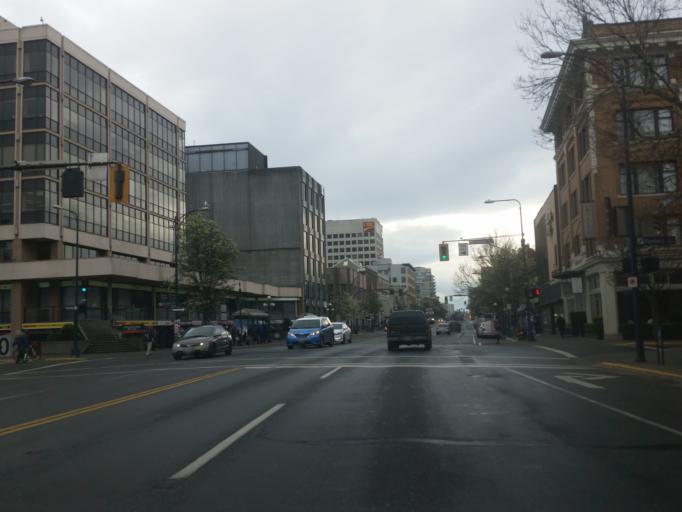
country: CA
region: British Columbia
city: Victoria
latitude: 48.4283
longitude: -123.3645
